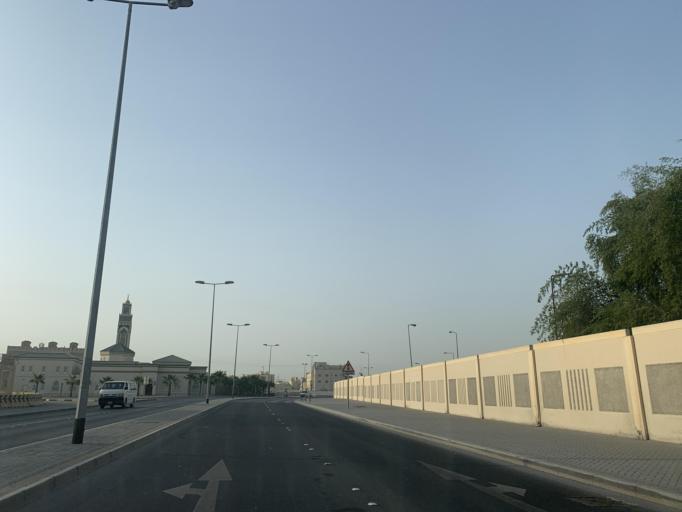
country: BH
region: Northern
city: Madinat `Isa
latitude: 26.1948
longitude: 50.5564
